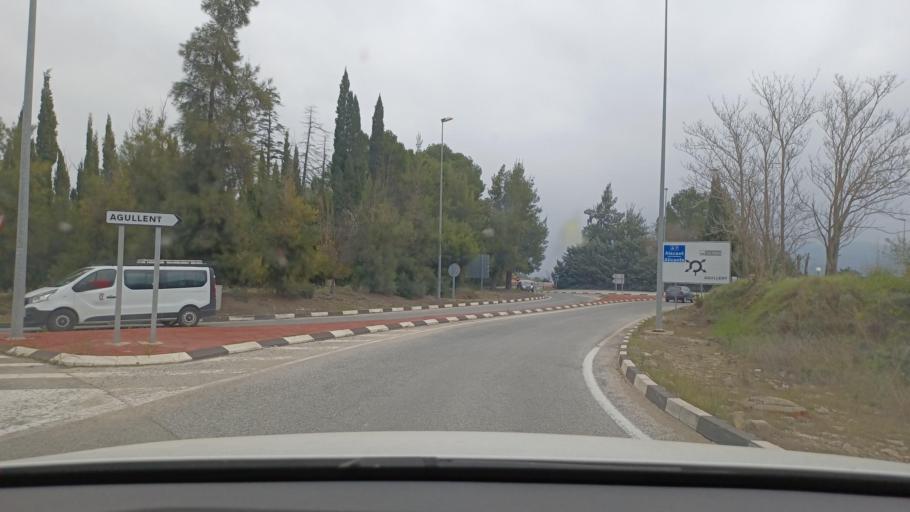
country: ES
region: Valencia
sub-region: Provincia de Valencia
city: Agullent
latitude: 38.8323
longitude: -0.5656
